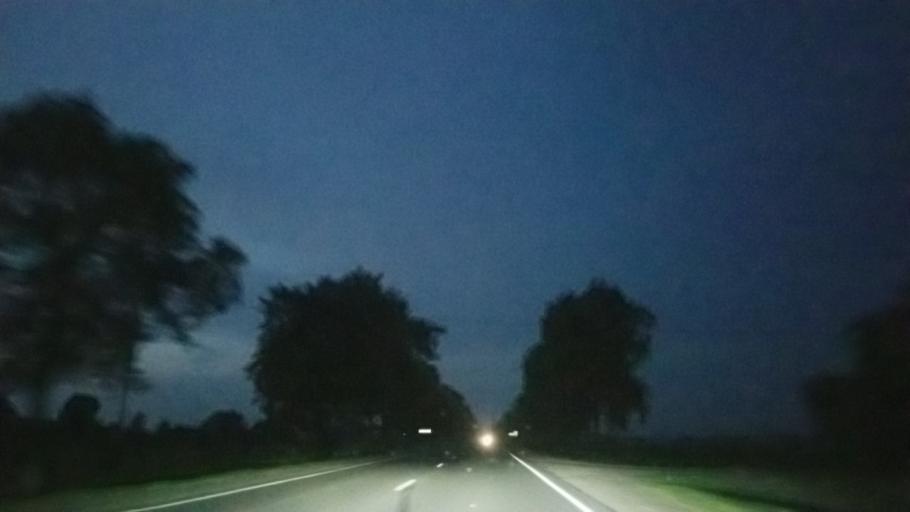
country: PL
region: Lublin Voivodeship
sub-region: Powiat bialski
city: Koden
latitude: 51.9445
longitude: 23.6681
